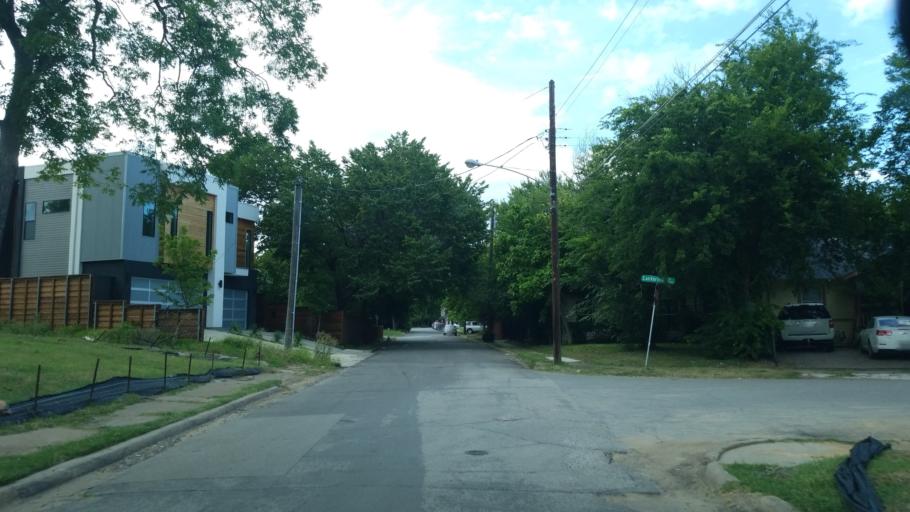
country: US
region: Texas
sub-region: Dallas County
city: Highland Park
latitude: 32.8061
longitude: -96.7826
